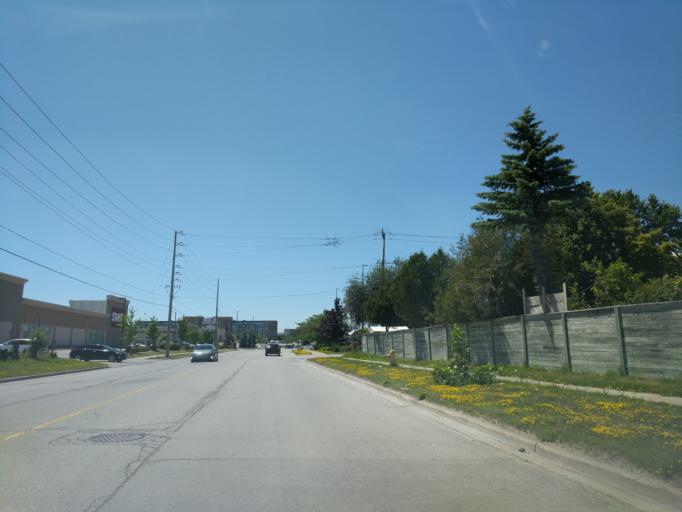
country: CA
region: Ontario
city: Ajax
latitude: 43.8436
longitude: -79.0663
